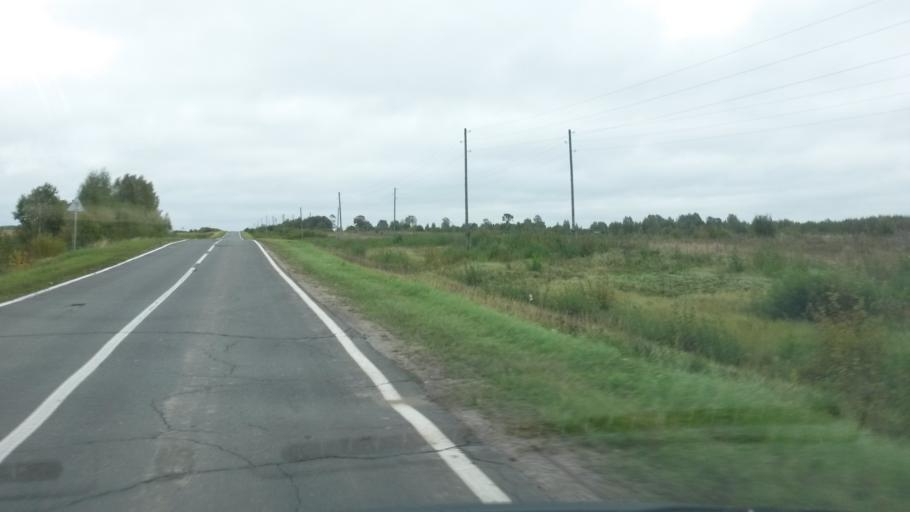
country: RU
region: Jaroslavl
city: Tutayev
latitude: 57.9508
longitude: 39.4328
